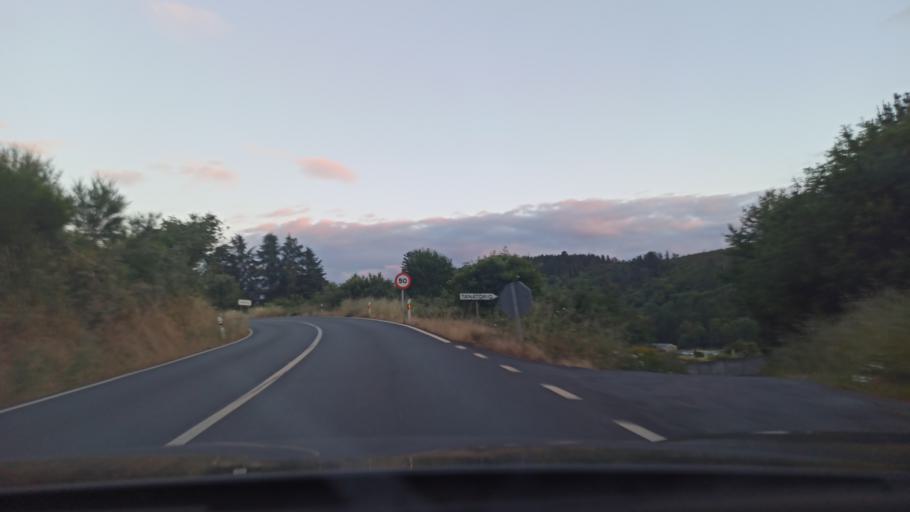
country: ES
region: Galicia
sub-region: Provincia de Lugo
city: Guntin
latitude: 42.8875
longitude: -7.7044
